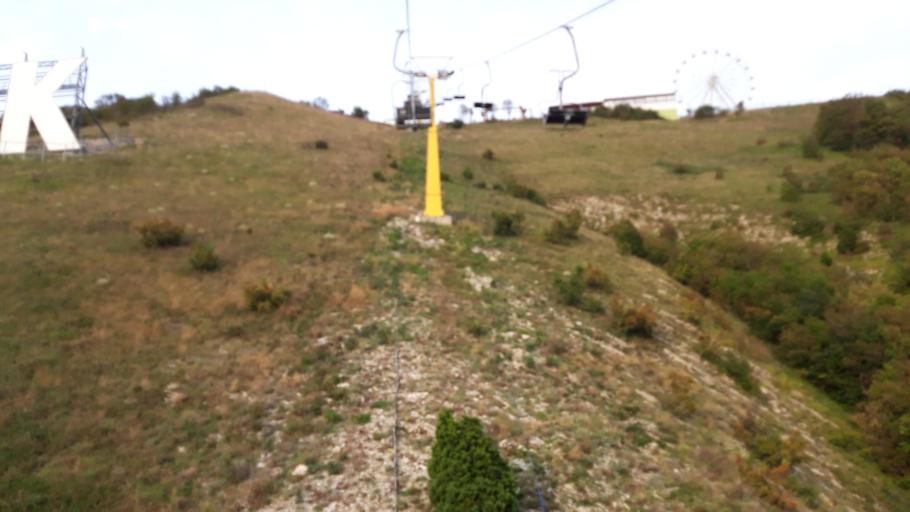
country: RU
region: Krasnodarskiy
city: Gelendzhik
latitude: 44.5837
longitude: 38.0999
